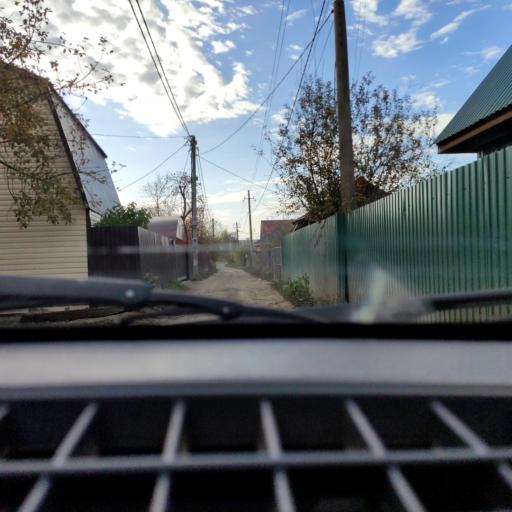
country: RU
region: Bashkortostan
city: Avdon
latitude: 54.7138
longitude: 55.8149
